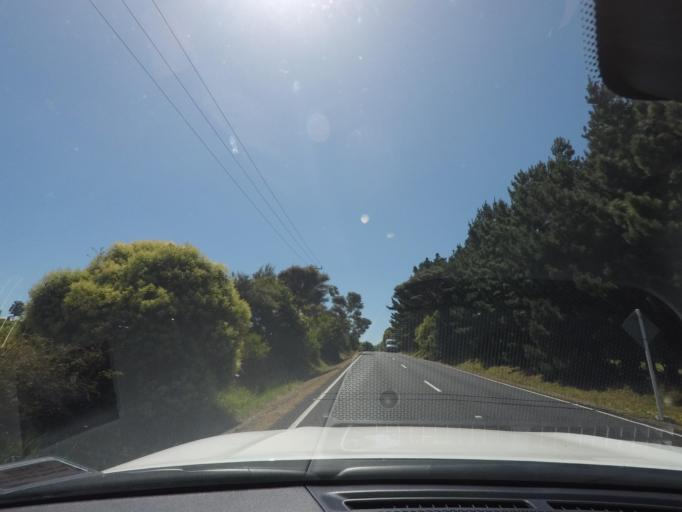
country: NZ
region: Auckland
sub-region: Auckland
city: Parakai
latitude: -36.6456
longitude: 174.3974
